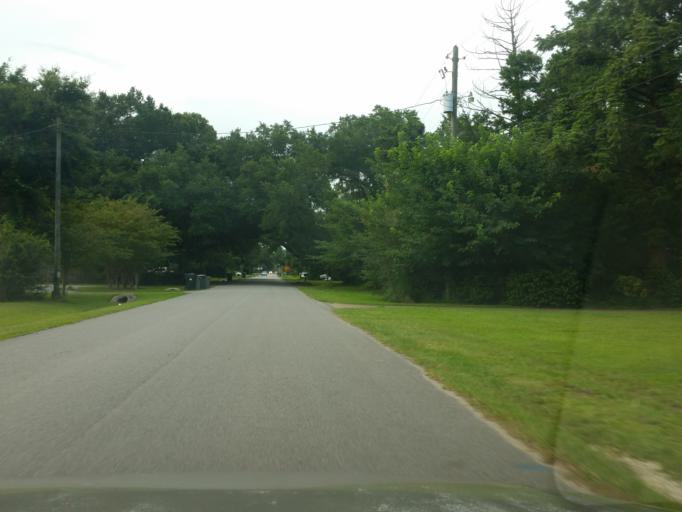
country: US
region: Florida
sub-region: Escambia County
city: Ferry Pass
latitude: 30.5070
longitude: -87.2274
